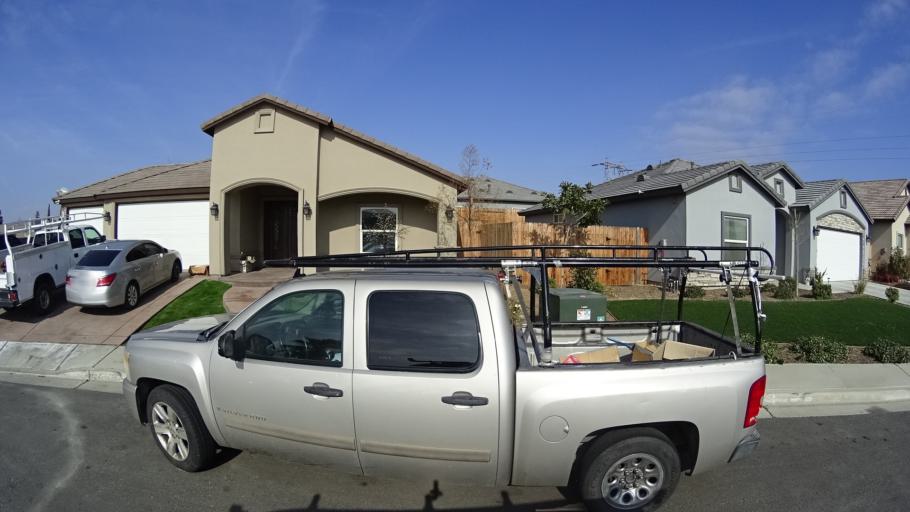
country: US
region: California
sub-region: Kern County
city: Oildale
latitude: 35.4006
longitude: -118.9252
